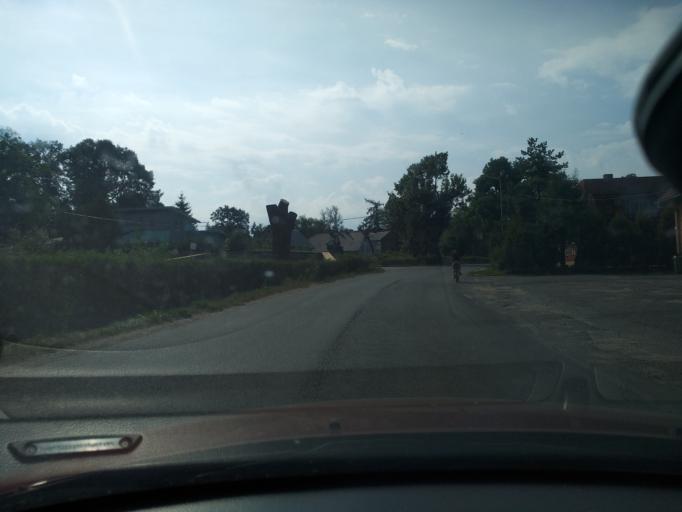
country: PL
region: Lower Silesian Voivodeship
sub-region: Powiat jeleniogorski
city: Stara Kamienica
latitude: 50.9195
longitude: 15.5729
